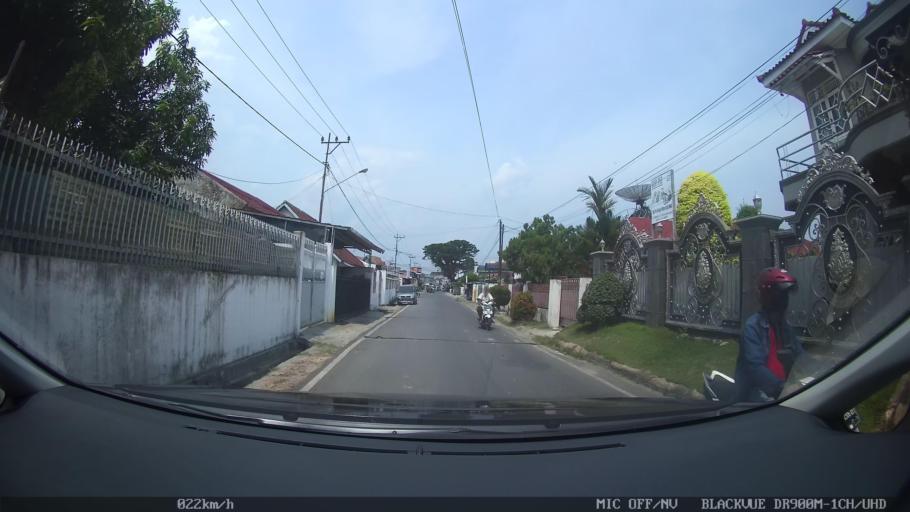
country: ID
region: Lampung
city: Bandarlampung
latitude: -5.4511
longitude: 105.2575
